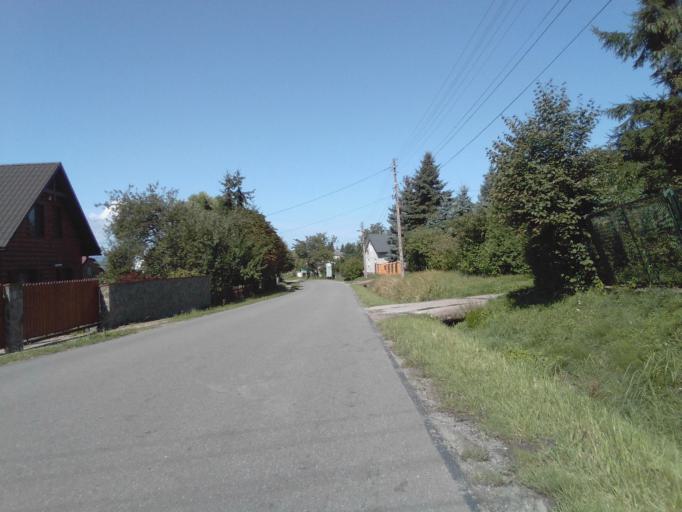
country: PL
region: Subcarpathian Voivodeship
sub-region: Powiat krosnienski
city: Chorkowka
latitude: 49.6050
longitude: 21.6611
